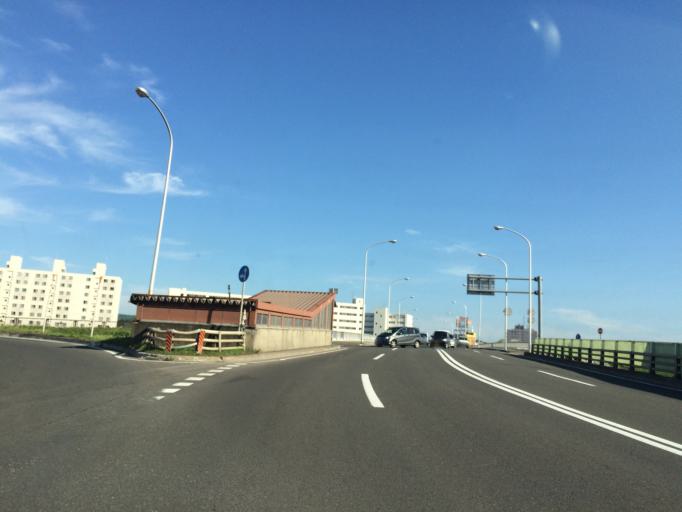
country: JP
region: Hokkaido
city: Sapporo
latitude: 43.0097
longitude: 141.3467
